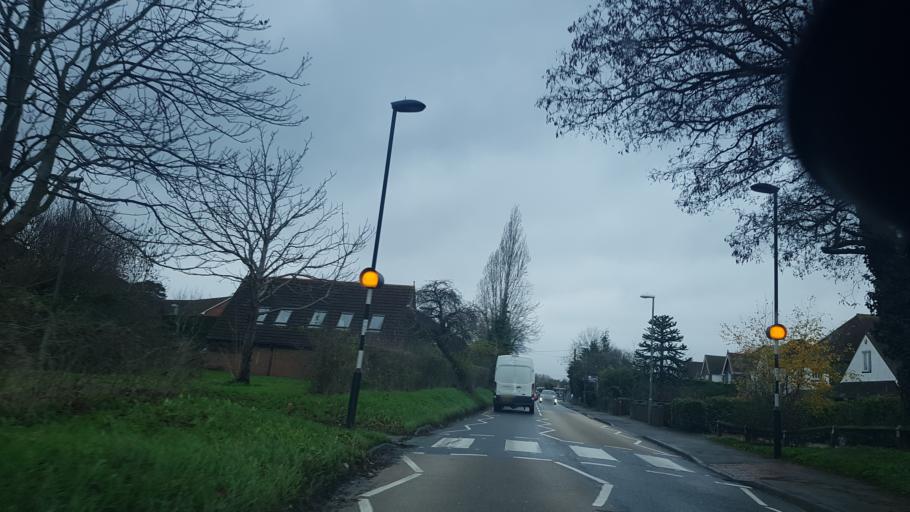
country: GB
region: England
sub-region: Surrey
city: Send
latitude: 51.2582
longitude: -0.5430
